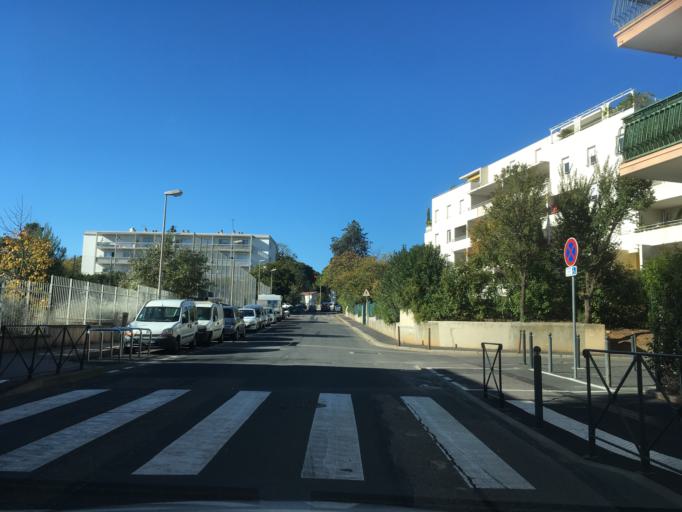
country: FR
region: Languedoc-Roussillon
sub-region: Departement de l'Herault
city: Montpellier
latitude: 43.6080
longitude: 3.8545
